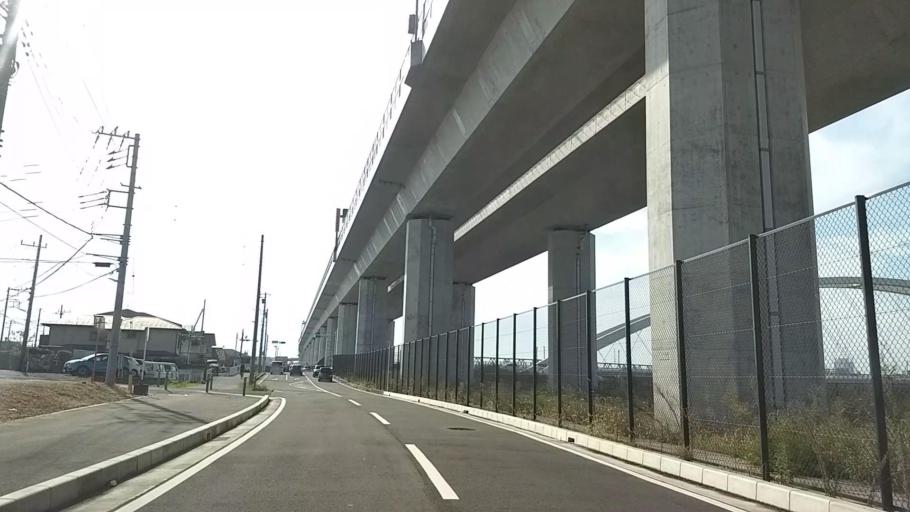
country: JP
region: Kanagawa
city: Atsugi
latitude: 35.4469
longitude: 139.3744
